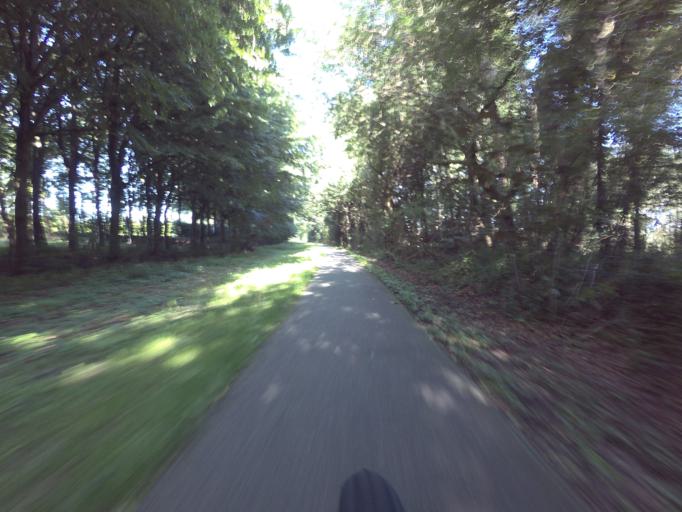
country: DK
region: Central Jutland
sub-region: Horsens Kommune
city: Horsens
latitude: 55.8797
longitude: 9.8205
